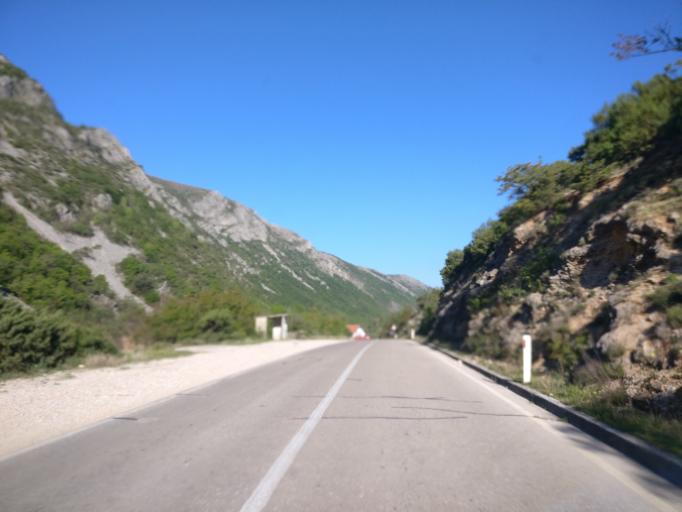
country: BA
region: Federation of Bosnia and Herzegovina
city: Stolac
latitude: 43.0763
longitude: 18.0252
